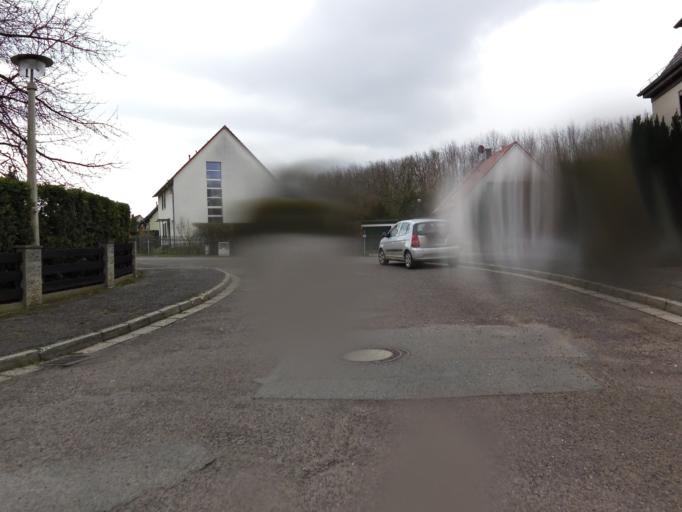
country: DE
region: Saxony
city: Markkleeberg
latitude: 51.2828
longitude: 12.4062
